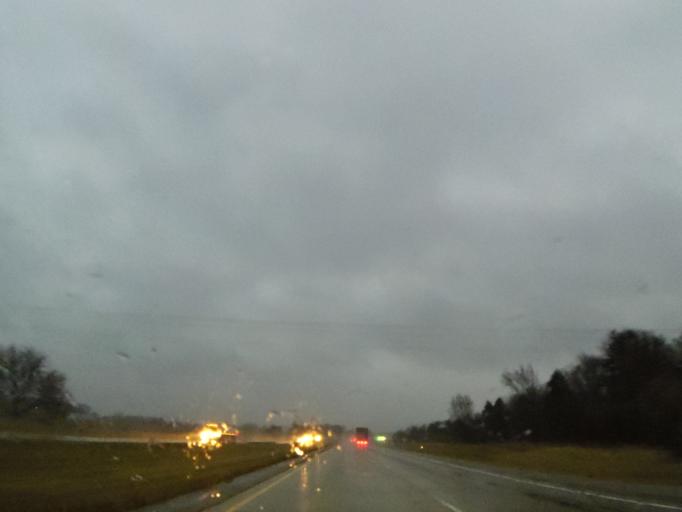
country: US
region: Minnesota
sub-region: Freeborn County
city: Albert Lea
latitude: 43.5857
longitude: -93.3576
